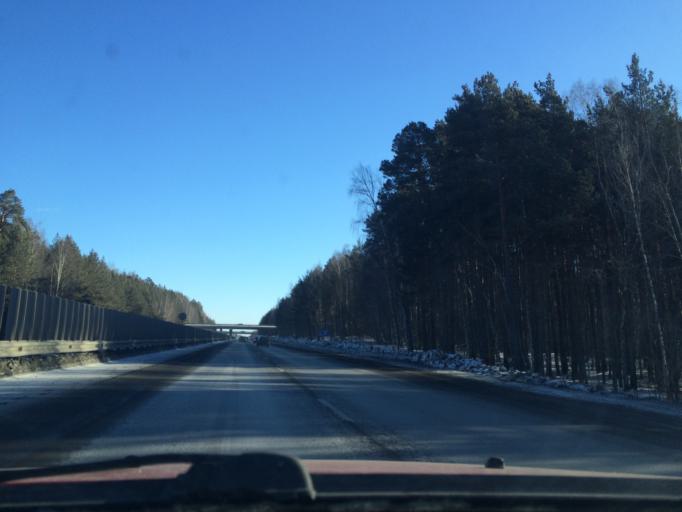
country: RU
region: Sverdlovsk
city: Istok
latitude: 56.8075
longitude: 60.7724
